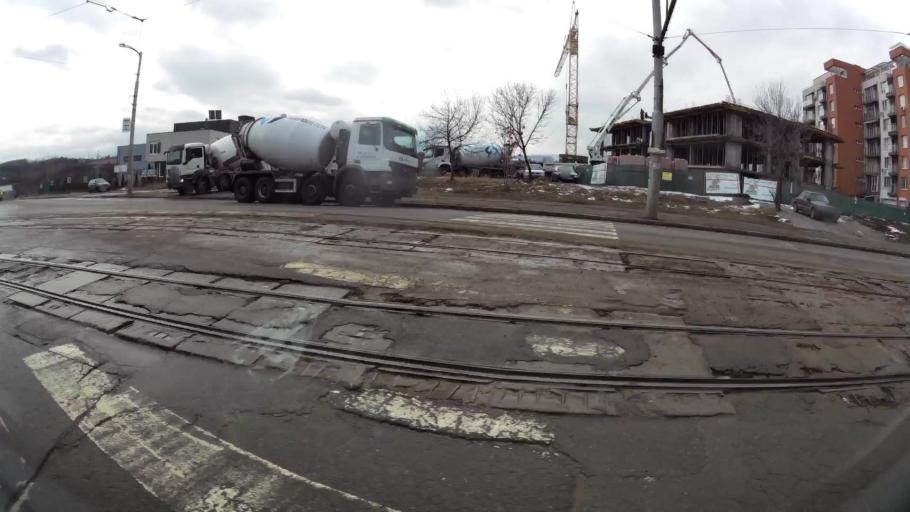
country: BG
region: Sofiya
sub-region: Obshtina Bozhurishte
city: Bozhurishte
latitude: 42.7098
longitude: 23.2445
